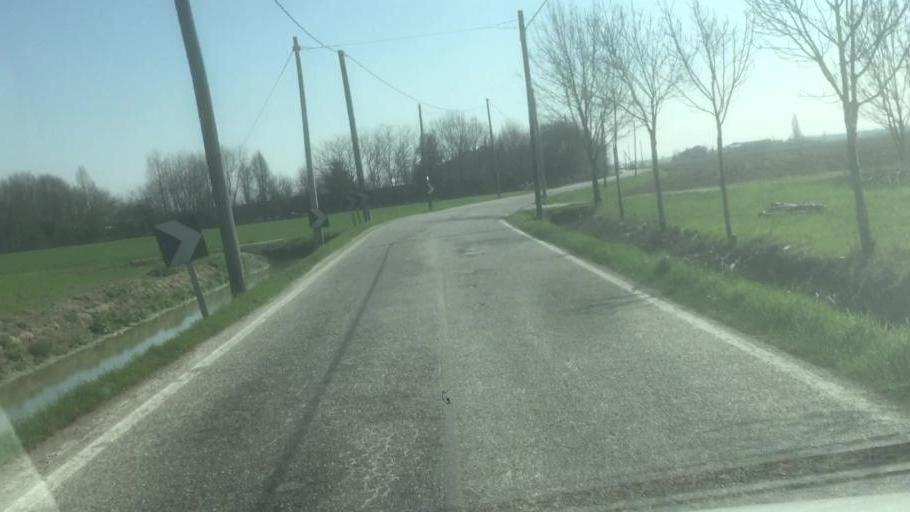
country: IT
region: Lombardy
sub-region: Provincia di Mantova
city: Ceresara
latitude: 45.2853
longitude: 10.5362
